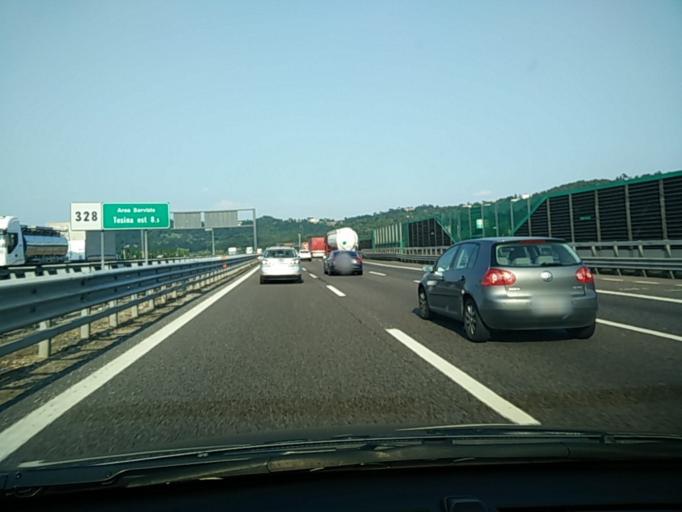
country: IT
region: Veneto
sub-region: Provincia di Vicenza
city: Arcugnano-Torri
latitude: 45.5180
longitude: 11.5176
